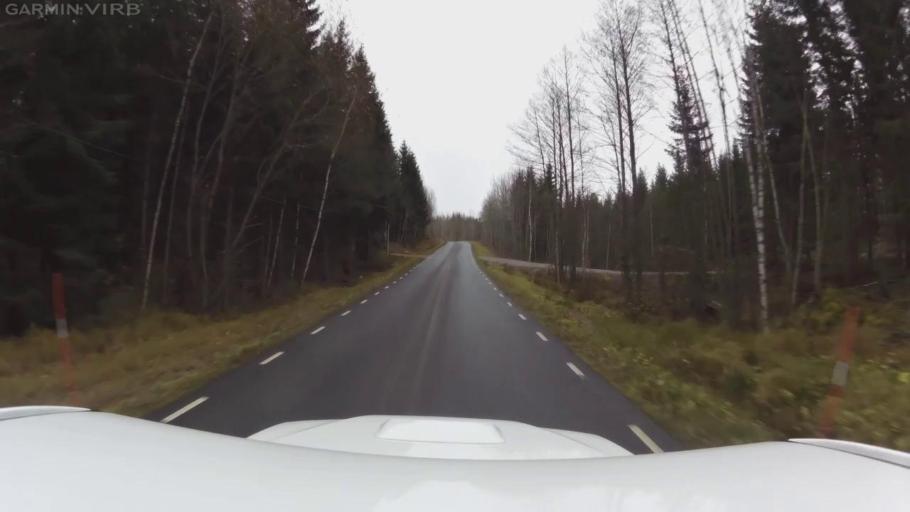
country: SE
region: OEstergoetland
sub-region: Mjolby Kommun
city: Mantorp
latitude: 58.1496
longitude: 15.3935
